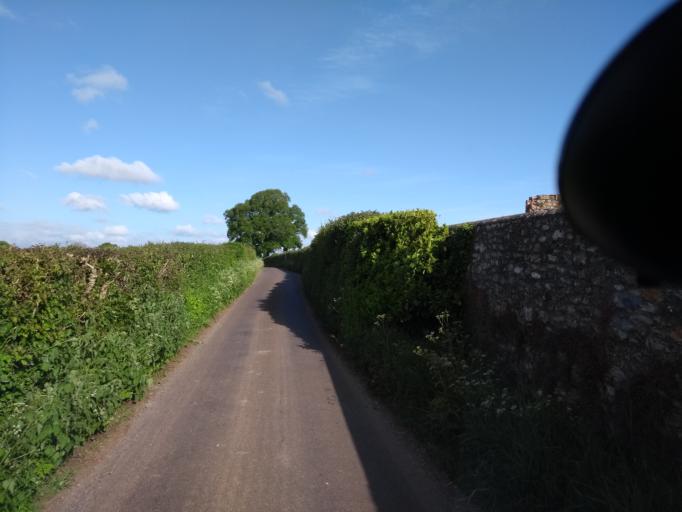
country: GB
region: England
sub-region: Somerset
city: Taunton
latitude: 50.9670
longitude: -3.1142
